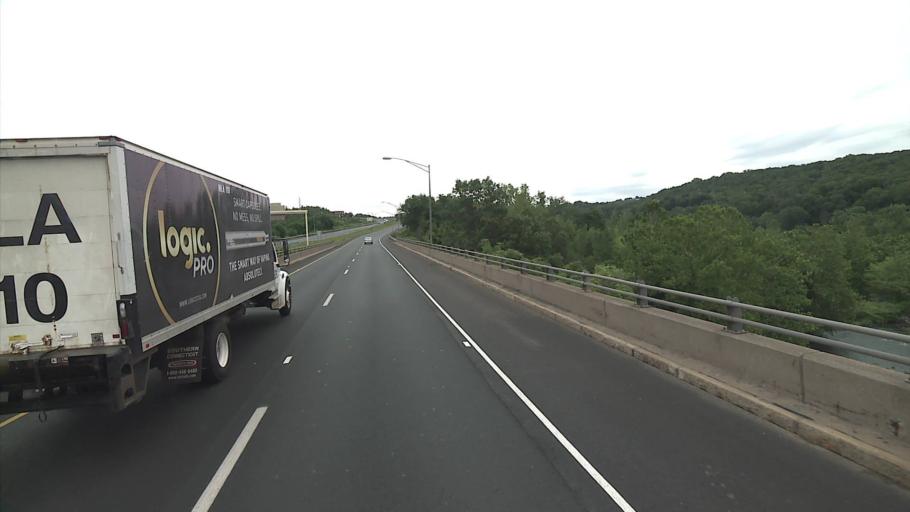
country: US
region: Connecticut
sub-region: New Haven County
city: Naugatuck
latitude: 41.5197
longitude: -73.0477
